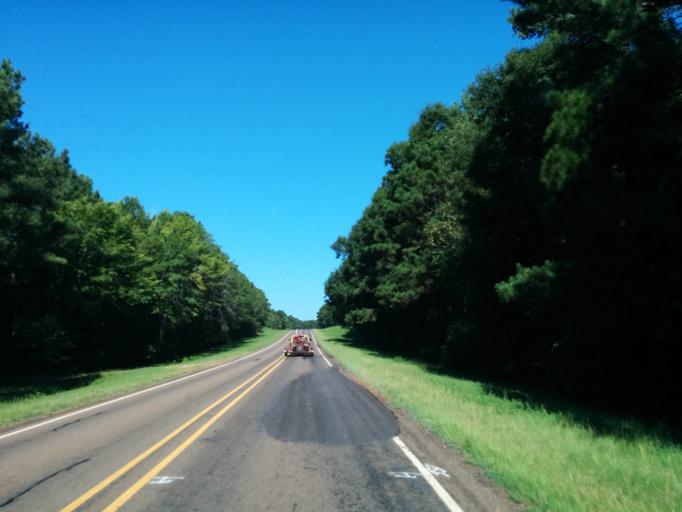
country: US
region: Texas
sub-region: Sabine County
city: Milam
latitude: 31.4291
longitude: -93.8035
